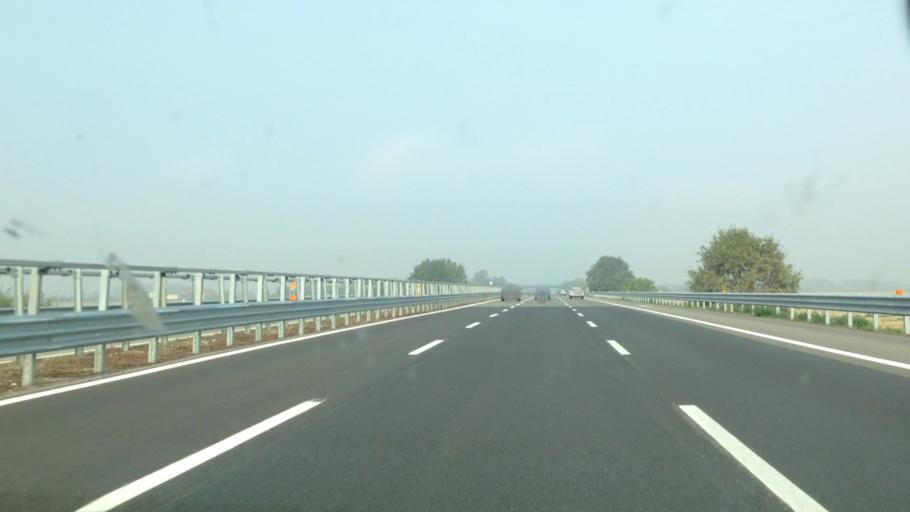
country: IT
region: Piedmont
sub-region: Provincia di Alessandria
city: Borgo San Martino
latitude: 45.0854
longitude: 8.5054
